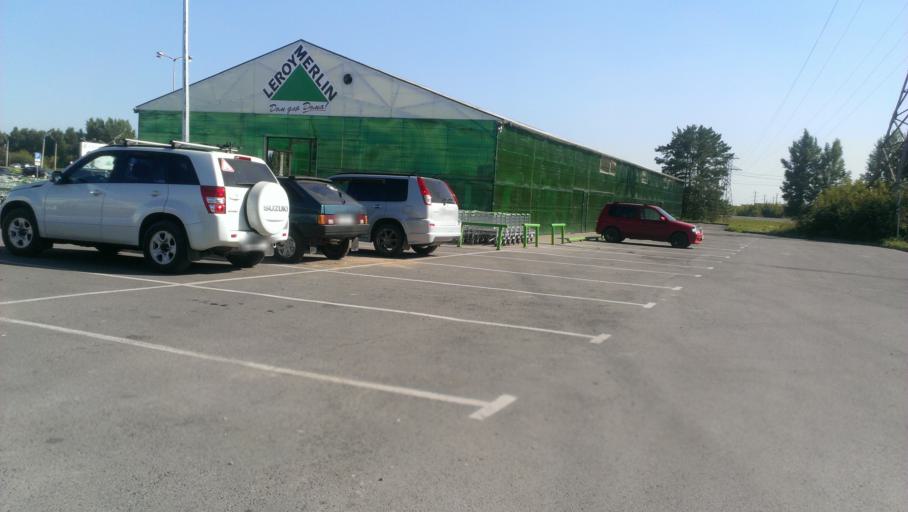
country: RU
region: Altai Krai
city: Novosilikatnyy
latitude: 53.3498
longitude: 83.6301
